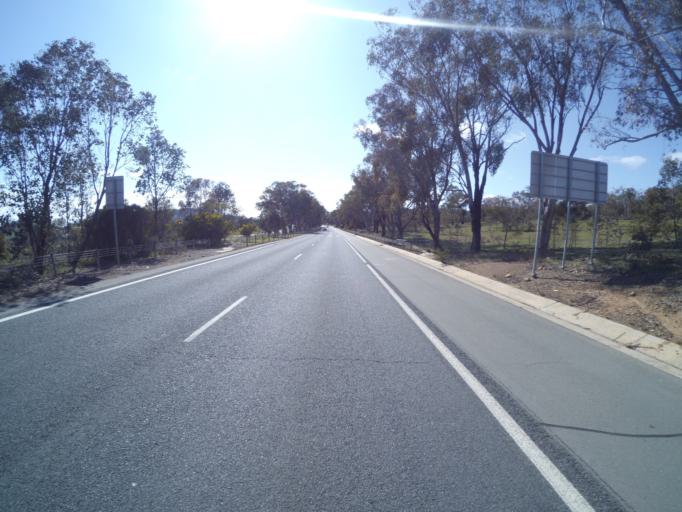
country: AU
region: Australian Capital Territory
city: Kaleen
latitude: -35.2217
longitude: 149.1751
